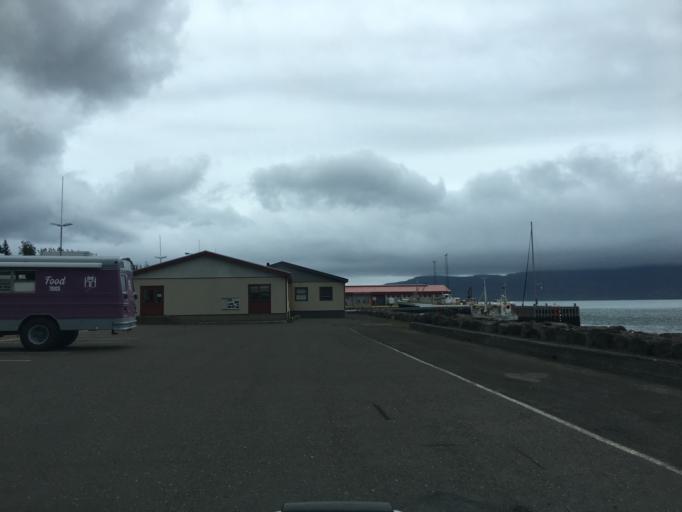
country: IS
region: East
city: Neskaupstadur
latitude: 65.1473
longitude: -13.6915
